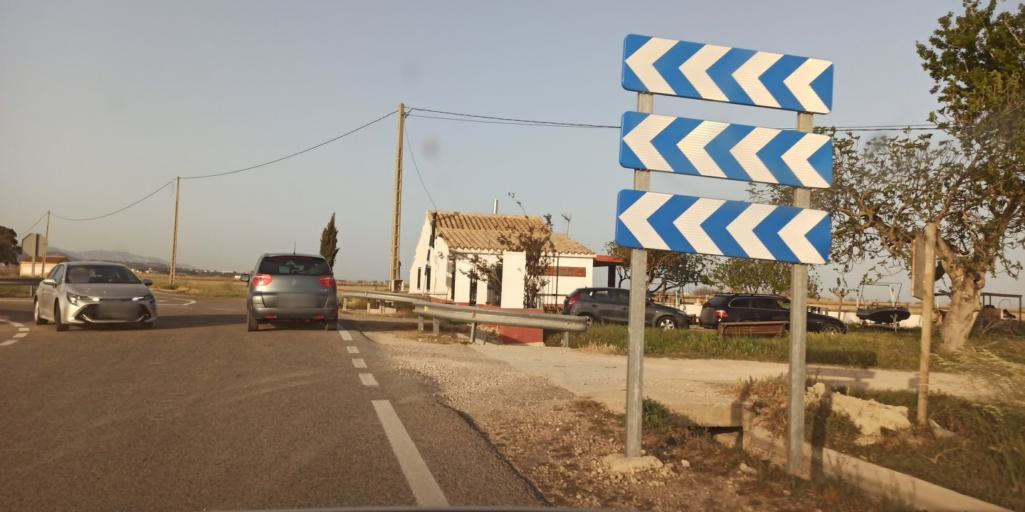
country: ES
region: Catalonia
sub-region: Provincia de Tarragona
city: L'Ampolla
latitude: 40.7907
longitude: 0.6973
